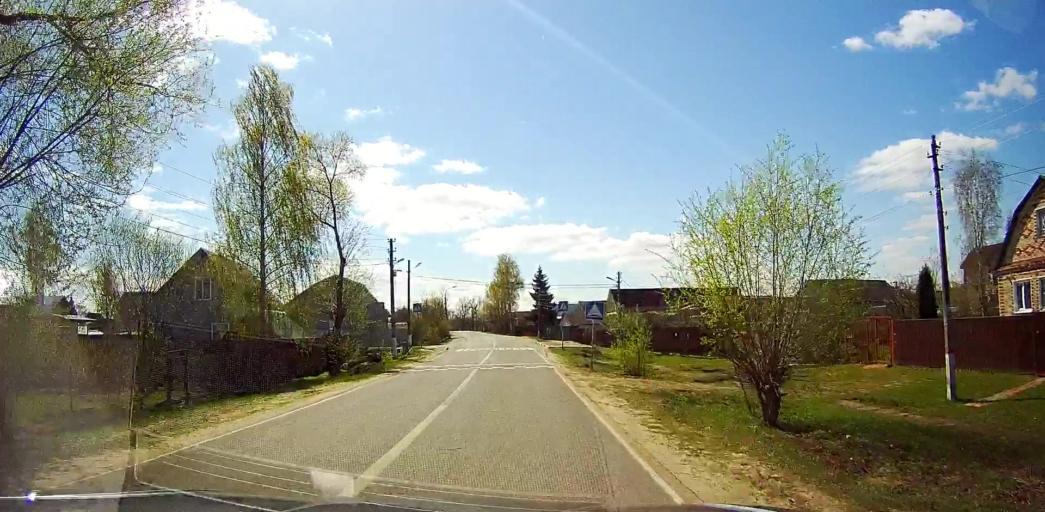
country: RU
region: Moskovskaya
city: Ramenskoye
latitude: 55.6246
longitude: 38.3020
